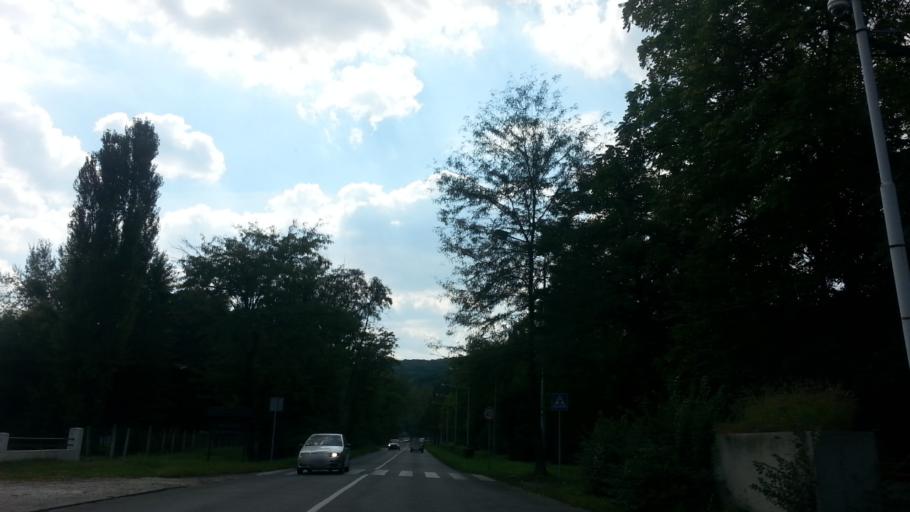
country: RS
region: Central Serbia
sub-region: Belgrade
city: Savski Venac
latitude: 44.7764
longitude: 20.4398
